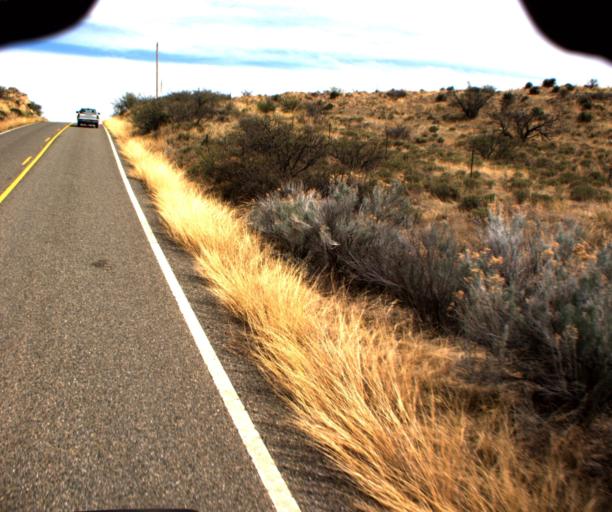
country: US
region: Arizona
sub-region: Cochise County
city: Willcox
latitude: 32.1686
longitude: -109.5913
